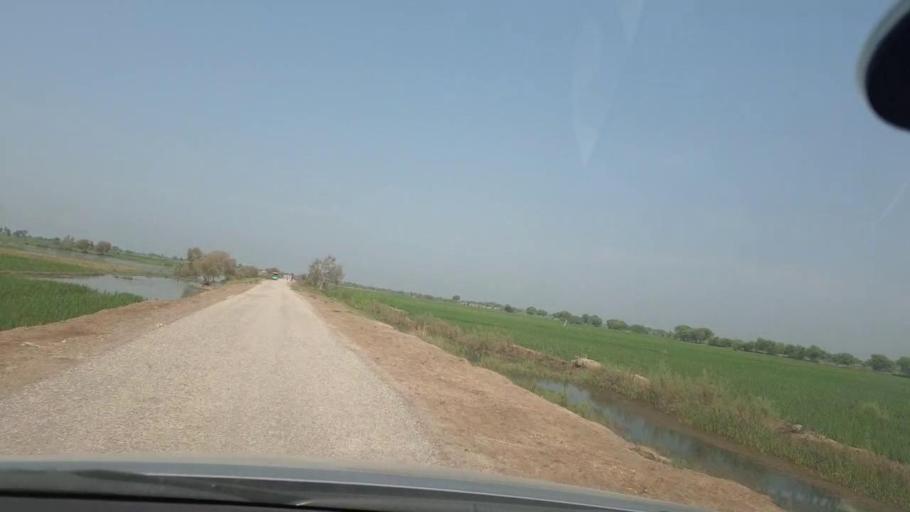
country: PK
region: Balochistan
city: Mehrabpur
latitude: 28.0682
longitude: 68.0560
